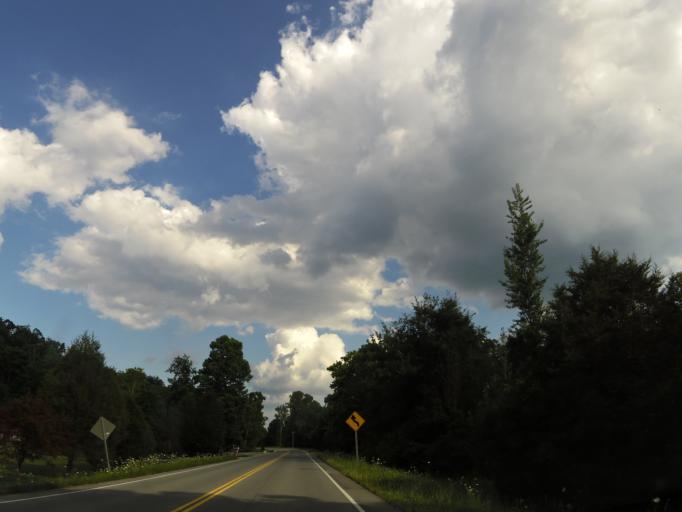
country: US
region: Tennessee
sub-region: Perry County
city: Linden
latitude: 35.6065
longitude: -87.7115
